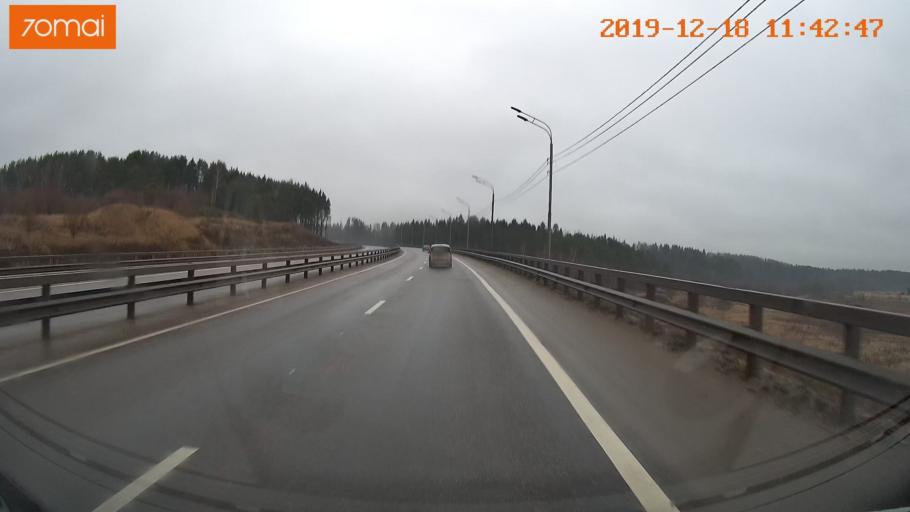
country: RU
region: Moskovskaya
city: Zvenigorod
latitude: 55.7275
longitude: 36.8799
